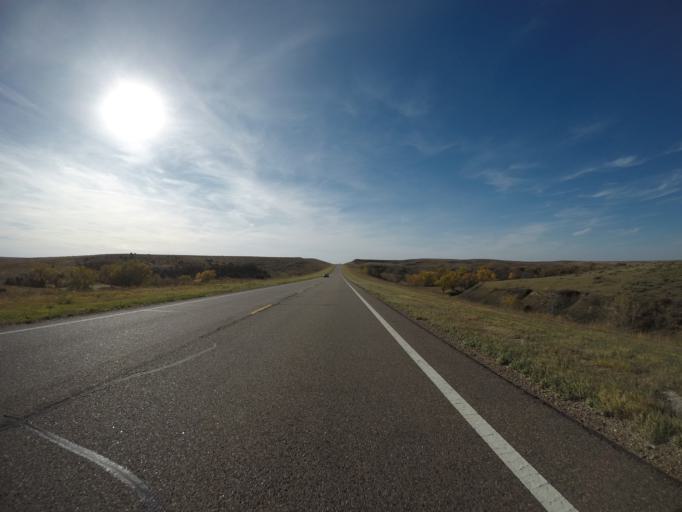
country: US
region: Kansas
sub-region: Rawlins County
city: Atwood
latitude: 39.8136
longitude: -100.9752
